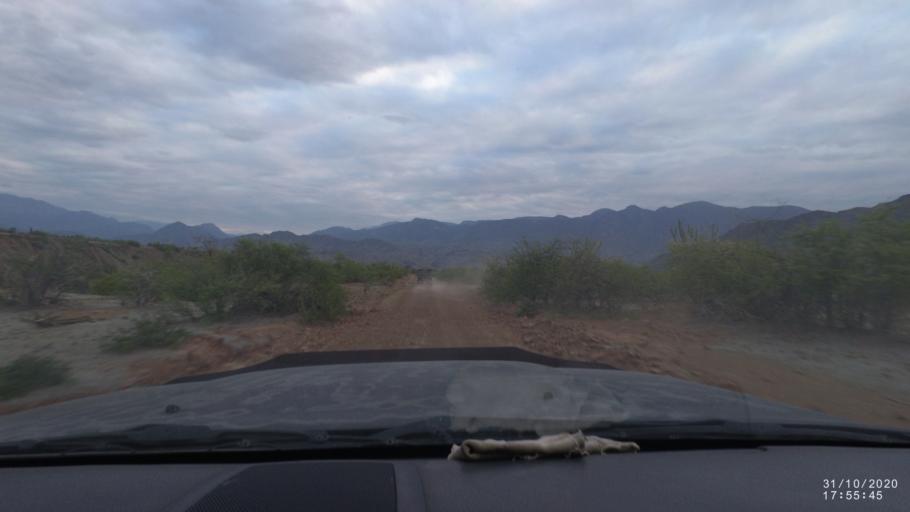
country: BO
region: Chuquisaca
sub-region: Provincia Zudanez
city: Mojocoya
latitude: -18.6463
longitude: -64.5285
